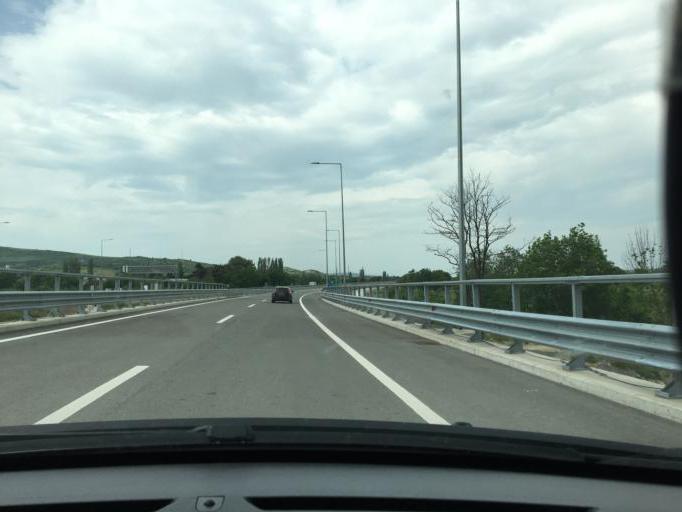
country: MK
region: Demir Kapija
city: Demir Kapija
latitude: 41.4096
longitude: 22.2516
